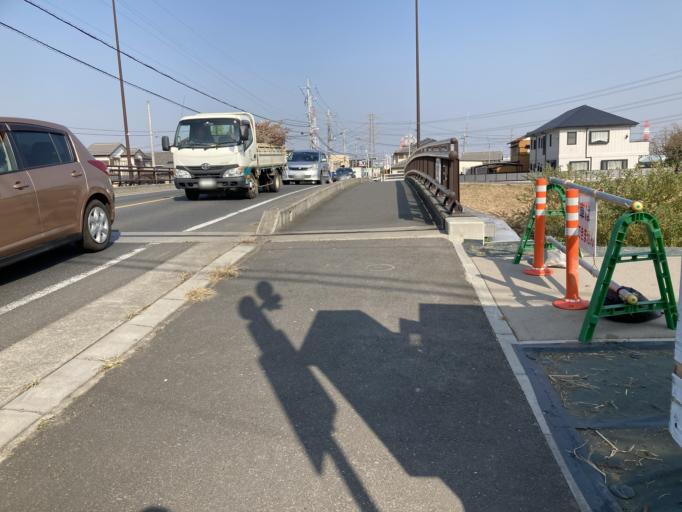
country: JP
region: Saitama
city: Koshigaya
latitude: 35.8870
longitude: 139.7412
